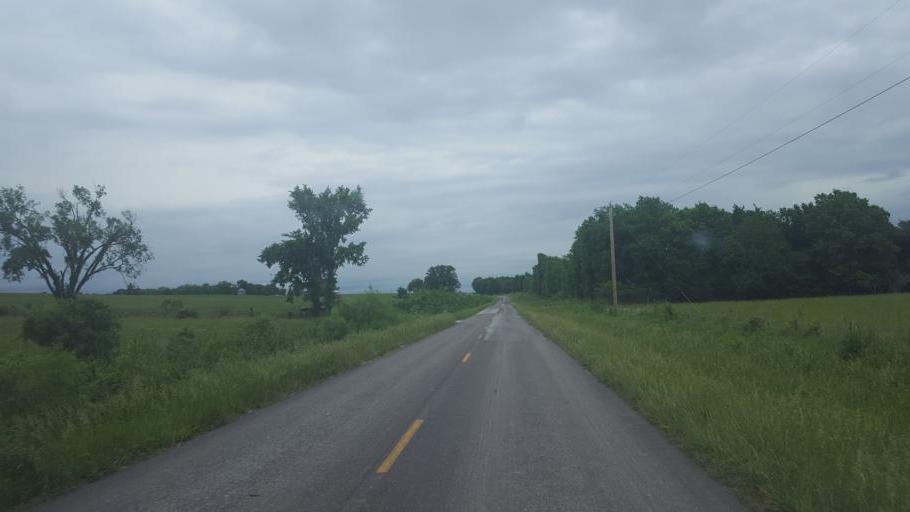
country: US
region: Missouri
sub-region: Moniteau County
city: California
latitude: 38.7773
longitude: -92.6050
